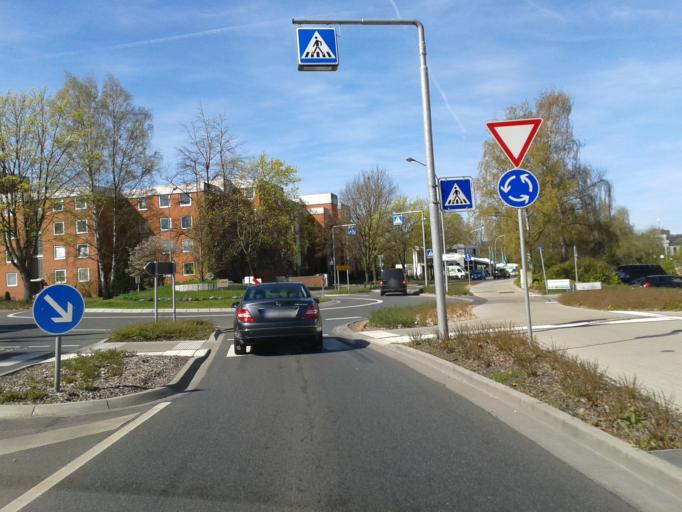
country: DE
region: Lower Saxony
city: Uelzen
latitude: 52.9591
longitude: 10.5620
